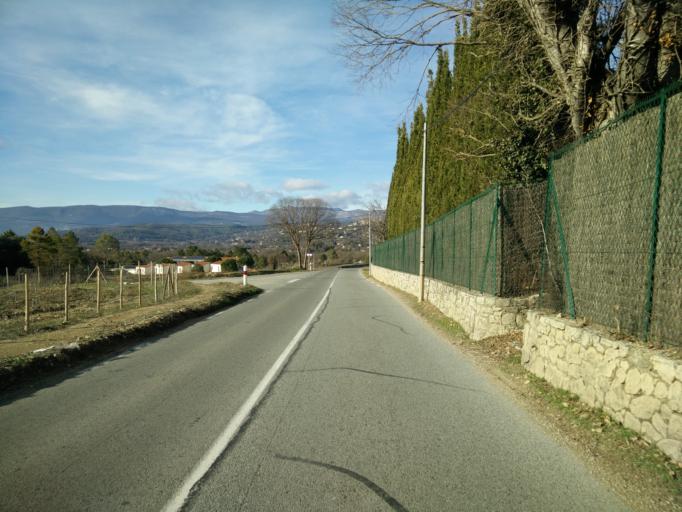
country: FR
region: Provence-Alpes-Cote d'Azur
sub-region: Departement du Var
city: Montauroux
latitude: 43.5964
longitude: 6.7877
